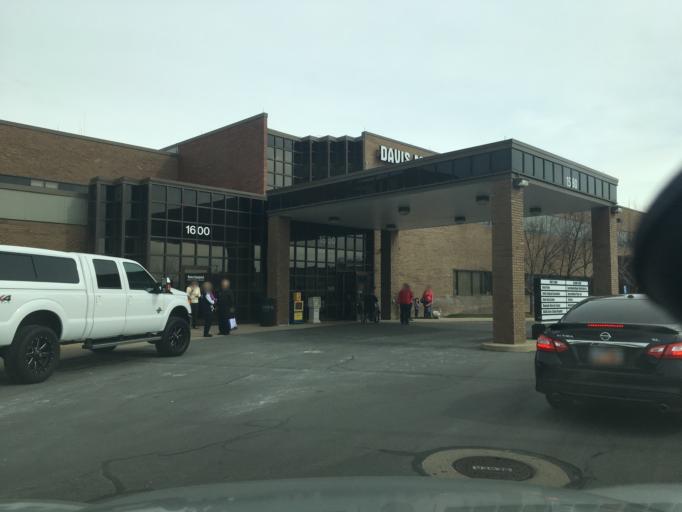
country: US
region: Utah
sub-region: Davis County
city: Hill Air Force Bace
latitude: 41.0905
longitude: -111.9950
